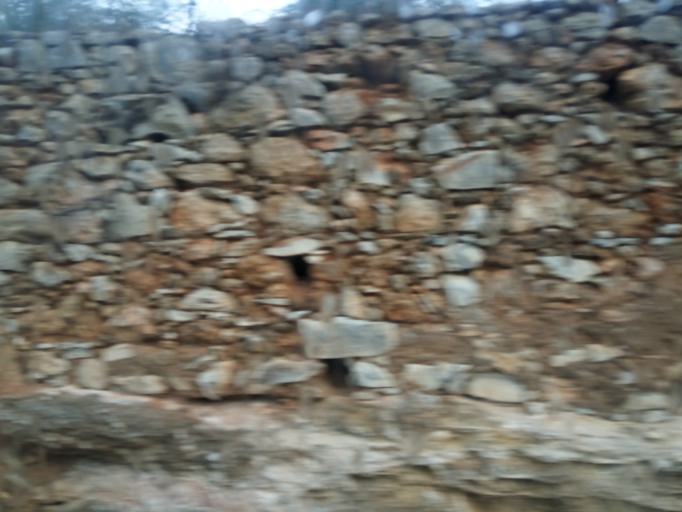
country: PT
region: Faro
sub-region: Faro
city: Santa Barbara de Nexe
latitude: 37.1048
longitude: -7.9700
